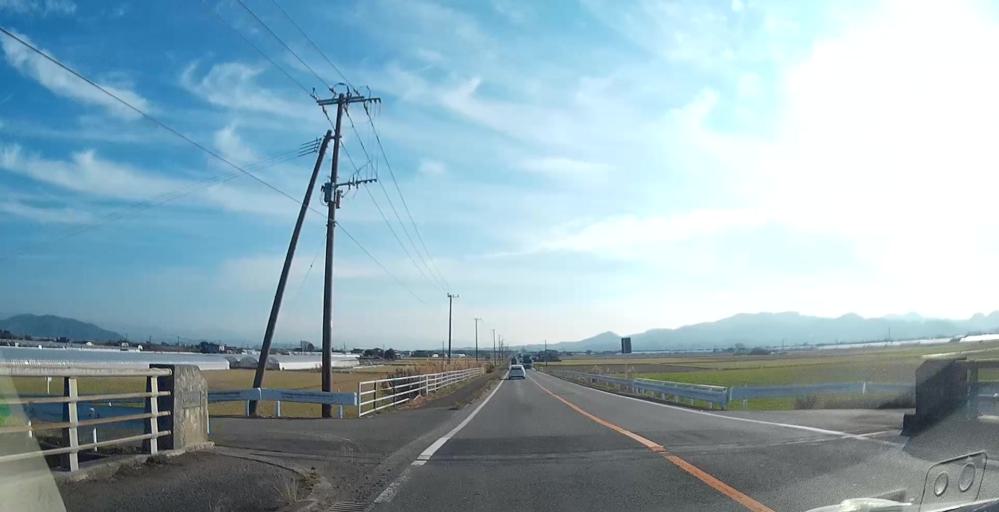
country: JP
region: Kumamoto
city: Uto
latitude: 32.7270
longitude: 130.6398
